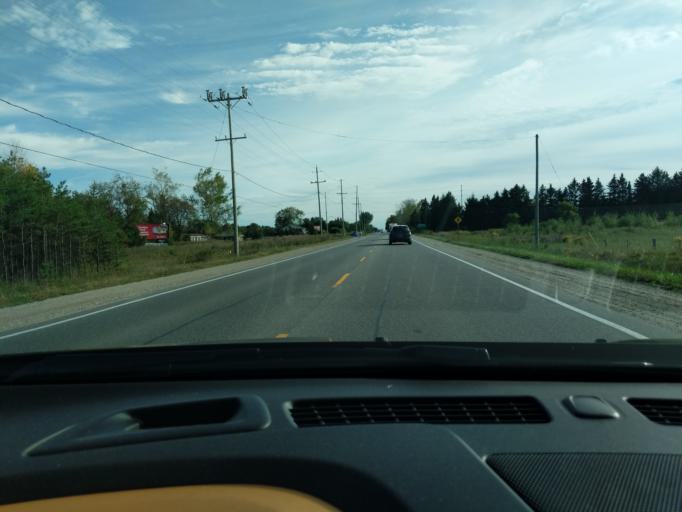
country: CA
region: Ontario
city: Wasaga Beach
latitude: 44.4368
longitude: -80.1002
